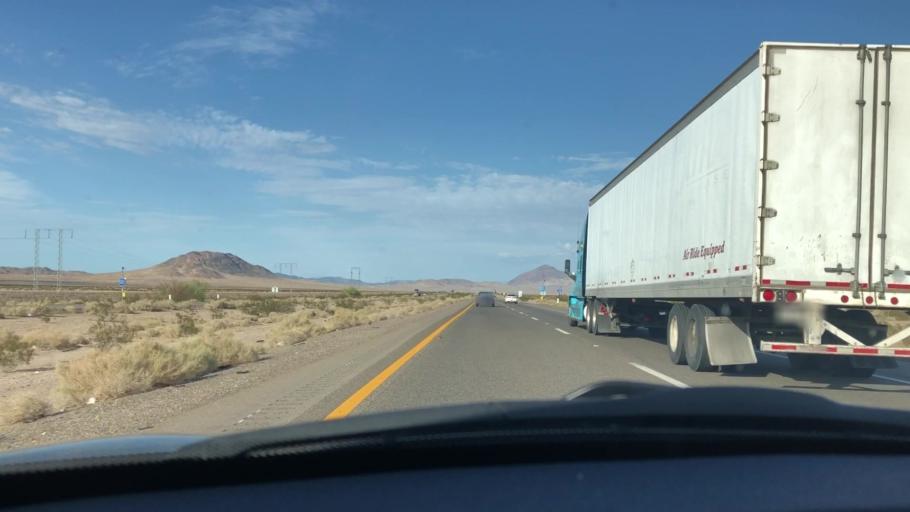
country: US
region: California
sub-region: San Bernardino County
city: Fort Irwin
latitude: 35.0127
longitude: -116.5261
